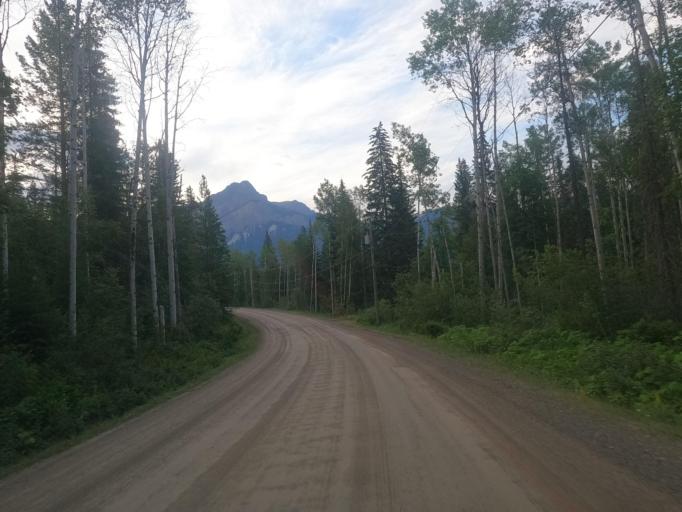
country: CA
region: British Columbia
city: Golden
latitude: 51.4445
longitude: -117.0307
